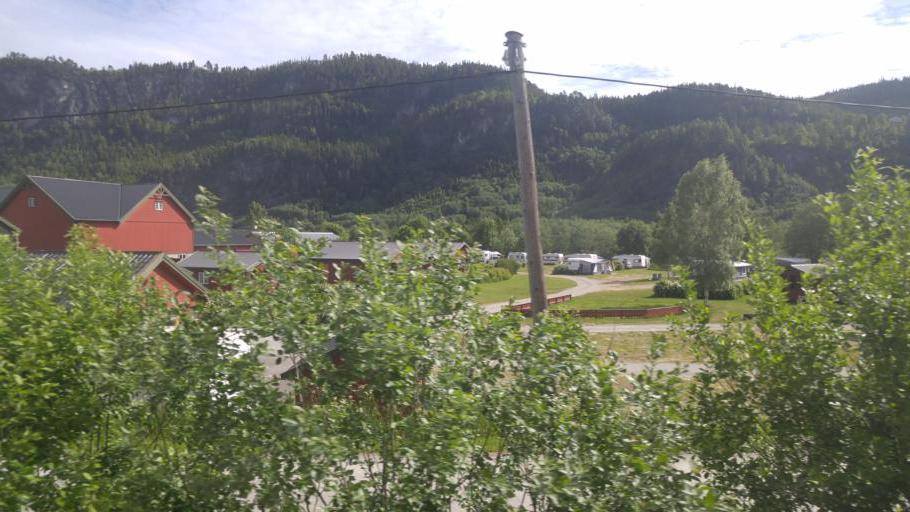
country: NO
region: Sor-Trondelag
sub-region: Midtre Gauldal
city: Storen
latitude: 63.0442
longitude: 10.2900
